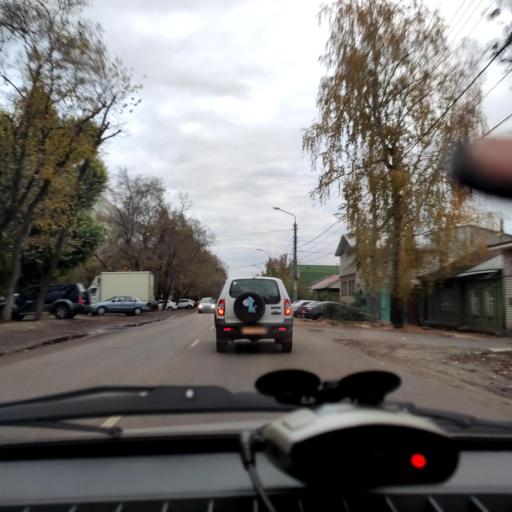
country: RU
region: Voronezj
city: Voronezh
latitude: 51.6362
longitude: 39.1885
